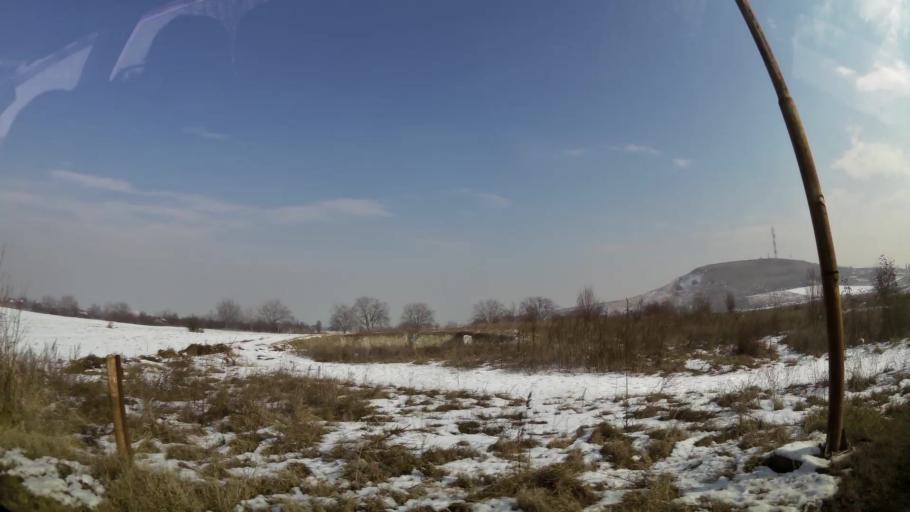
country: MK
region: Suto Orizari
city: Suto Orizare
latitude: 42.0203
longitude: 21.3876
